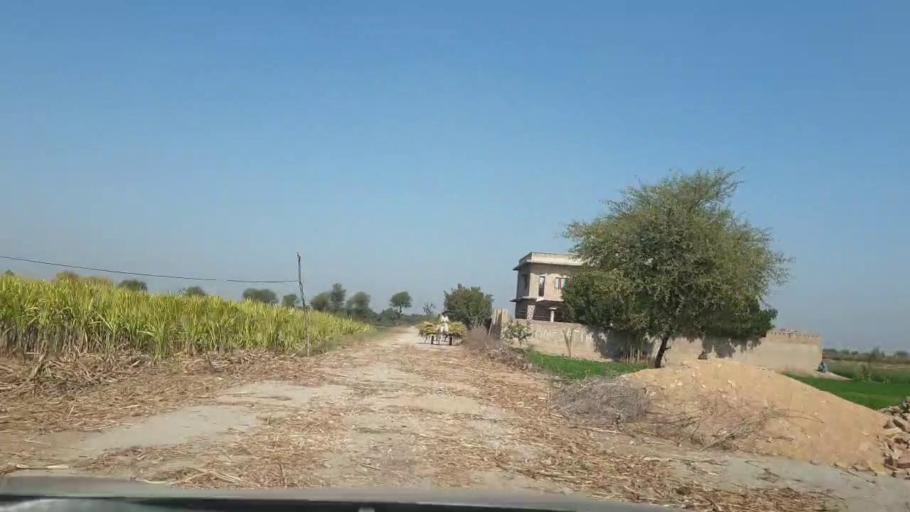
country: PK
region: Sindh
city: Tando Adam
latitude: 25.6166
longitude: 68.6462
